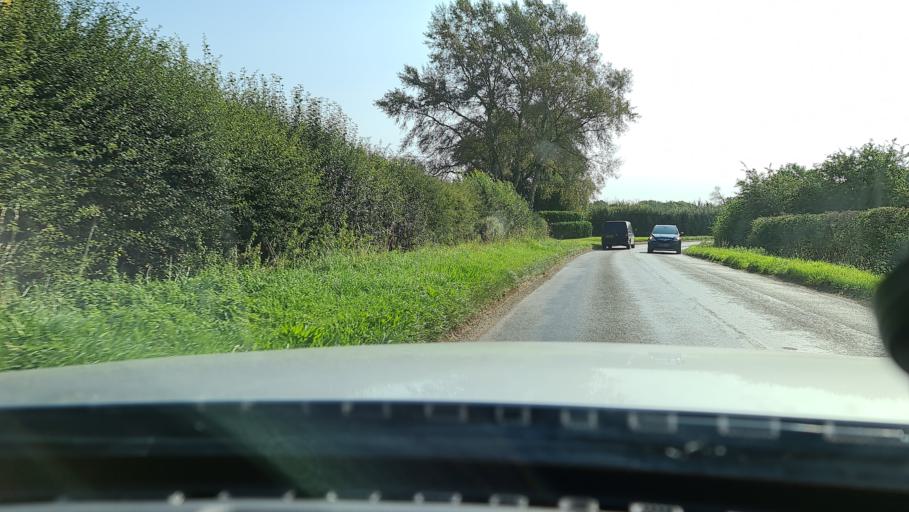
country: GB
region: England
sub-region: Oxfordshire
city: Adderbury
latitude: 52.0295
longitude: -1.2827
